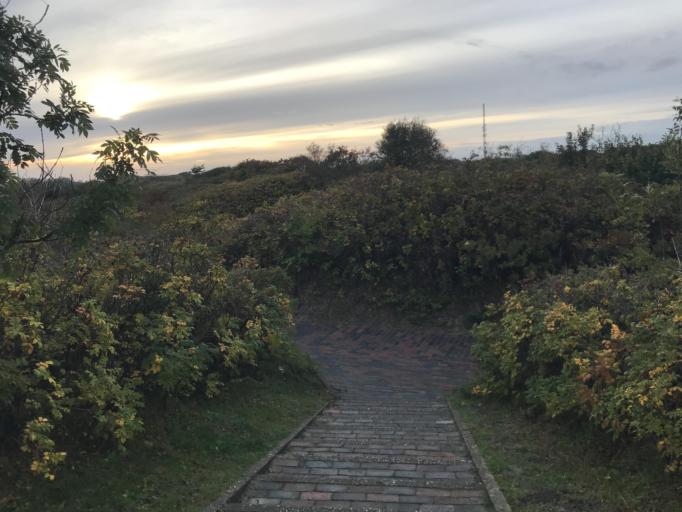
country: DE
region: Lower Saxony
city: Borkum
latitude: 53.5769
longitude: 6.6827
